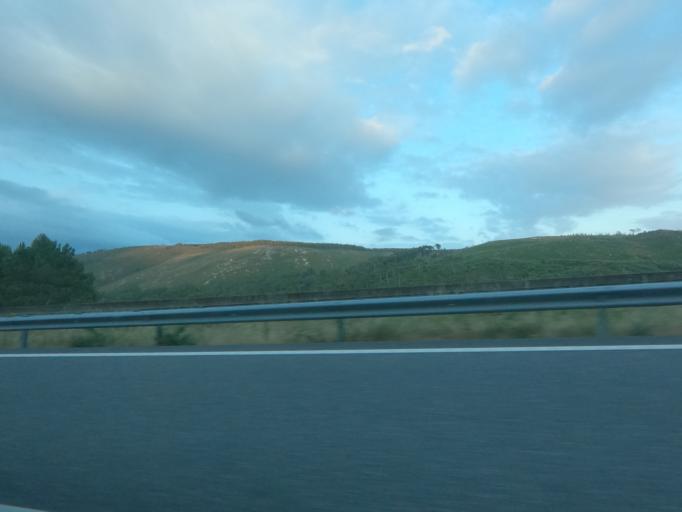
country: ES
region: Galicia
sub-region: Provincia de Ourense
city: Melon
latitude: 42.2382
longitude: -8.2291
